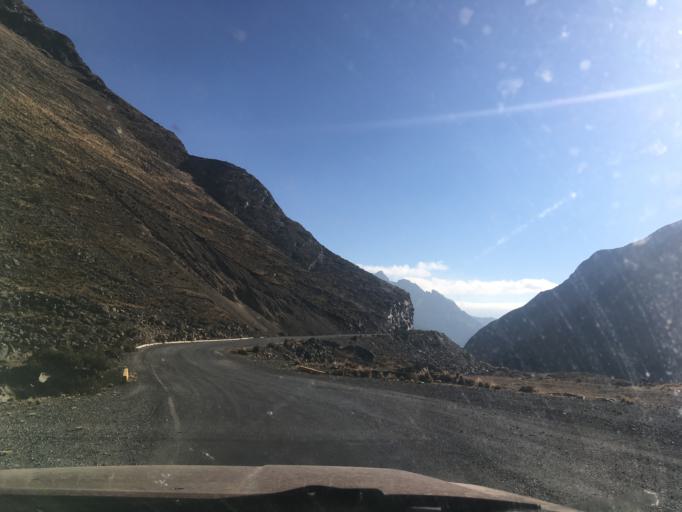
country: BO
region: La Paz
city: Quime
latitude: -17.0219
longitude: -67.2812
